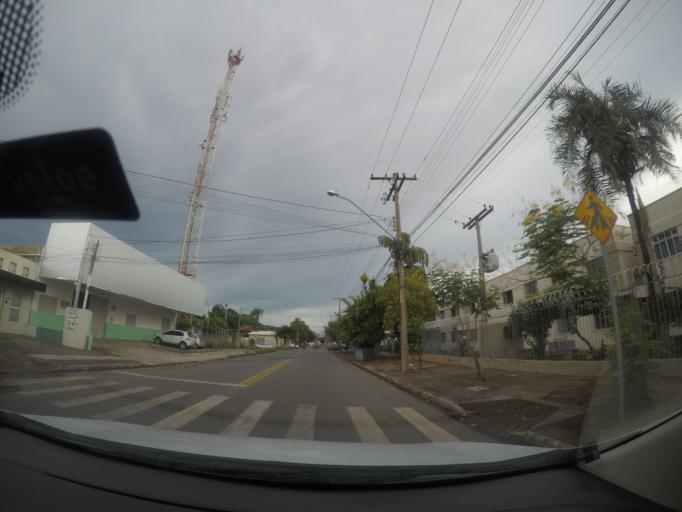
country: BR
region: Goias
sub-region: Goiania
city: Goiania
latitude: -16.7059
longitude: -49.3073
